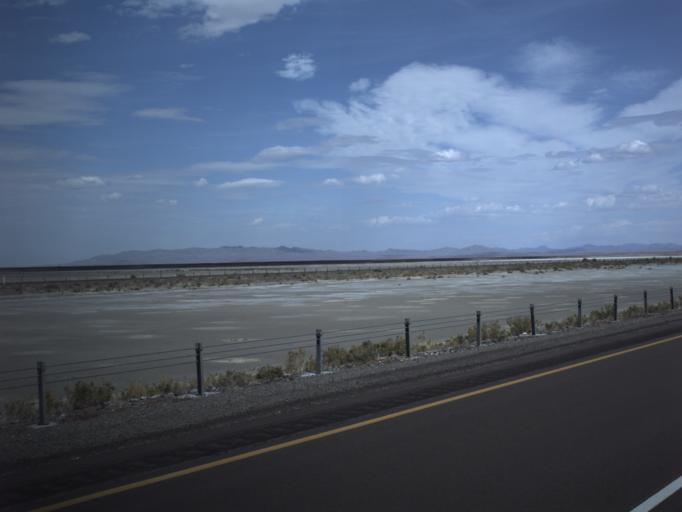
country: US
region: Utah
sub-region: Tooele County
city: Wendover
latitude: 40.7278
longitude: -113.3557
